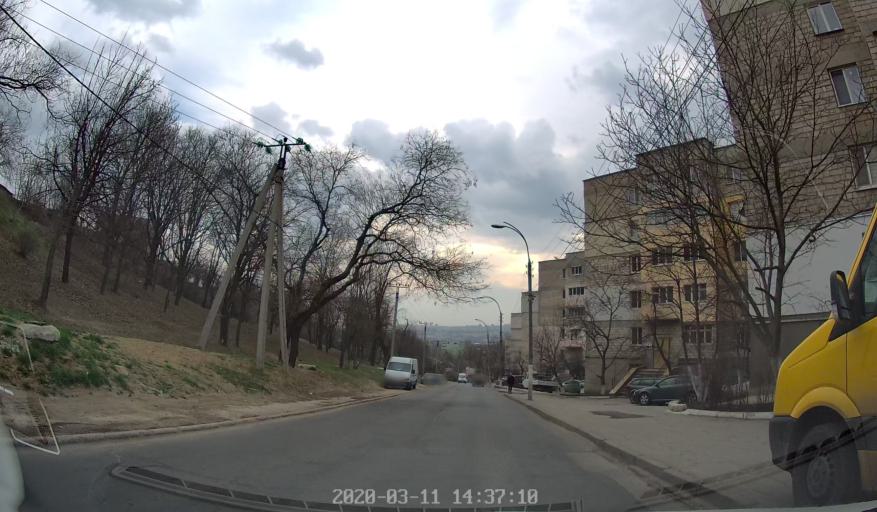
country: MD
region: Chisinau
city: Chisinau
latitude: 47.0234
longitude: 28.8759
